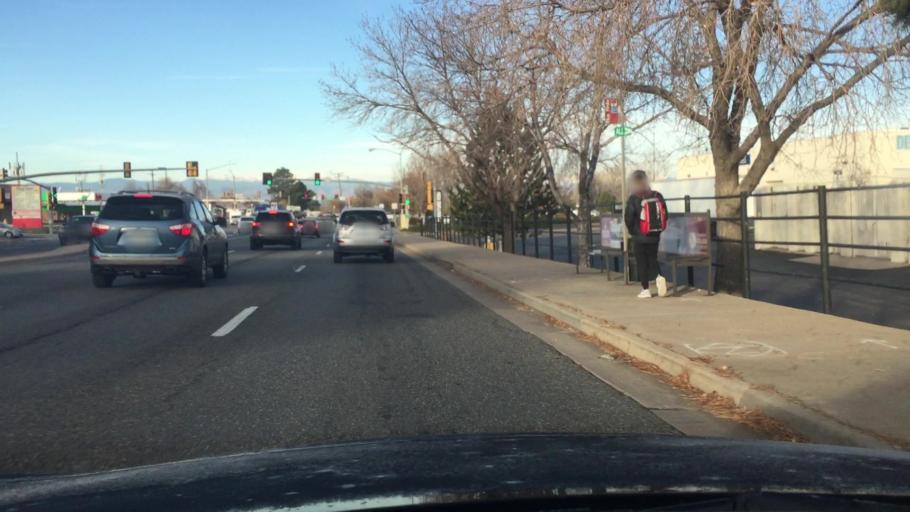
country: US
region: Colorado
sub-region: Arapahoe County
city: Dove Valley
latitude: 39.6387
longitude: -104.8263
